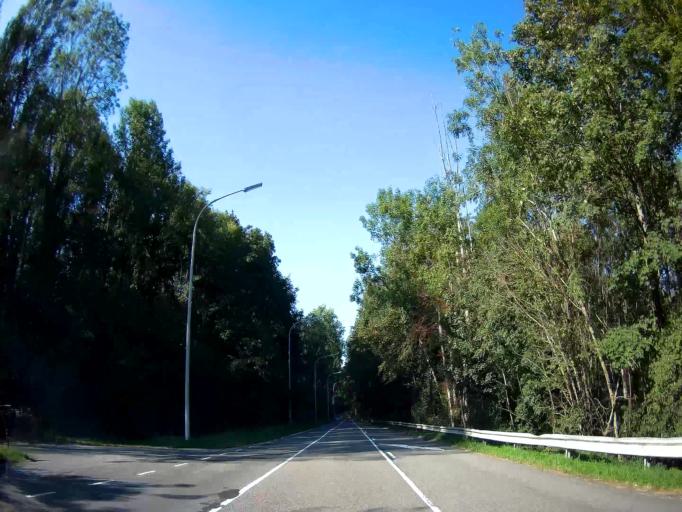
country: BE
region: Wallonia
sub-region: Province de Namur
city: Dinant
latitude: 50.2412
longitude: 4.9677
